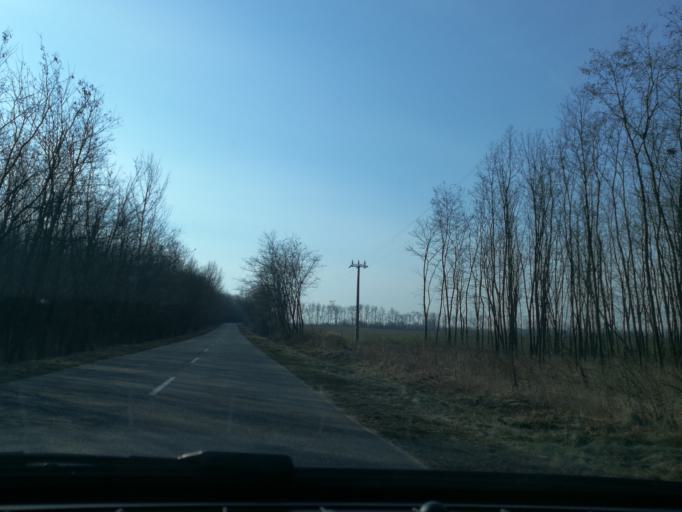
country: HU
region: Szabolcs-Szatmar-Bereg
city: Levelek
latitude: 47.9938
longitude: 21.9674
